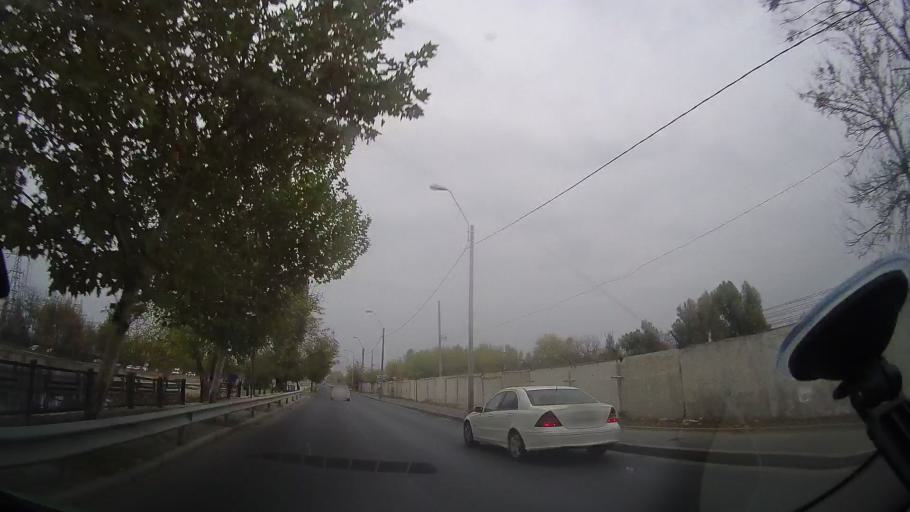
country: RO
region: Ilfov
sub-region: Comuna Popesti-Leordeni
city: Popesti-Leordeni
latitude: 44.4017
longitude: 26.1490
